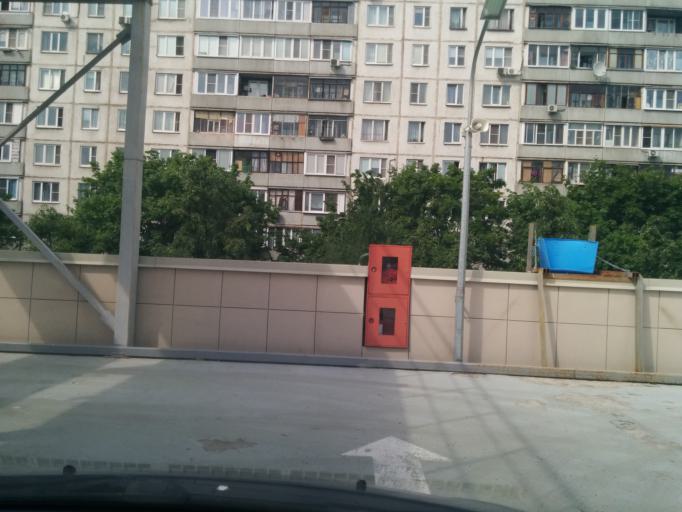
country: RU
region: Moscow
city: Bibirevo
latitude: 55.8902
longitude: 37.5941
